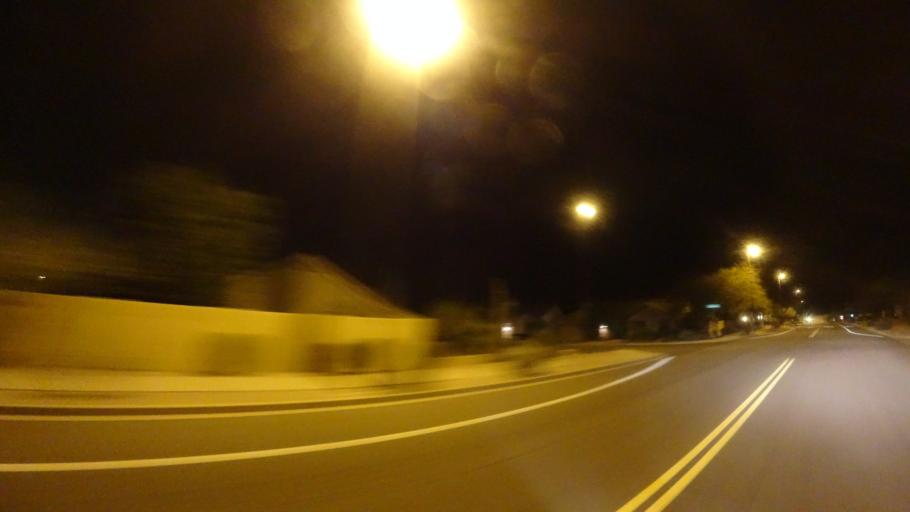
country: US
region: Arizona
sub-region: Maricopa County
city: Fountain Hills
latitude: 33.4929
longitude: -111.6994
